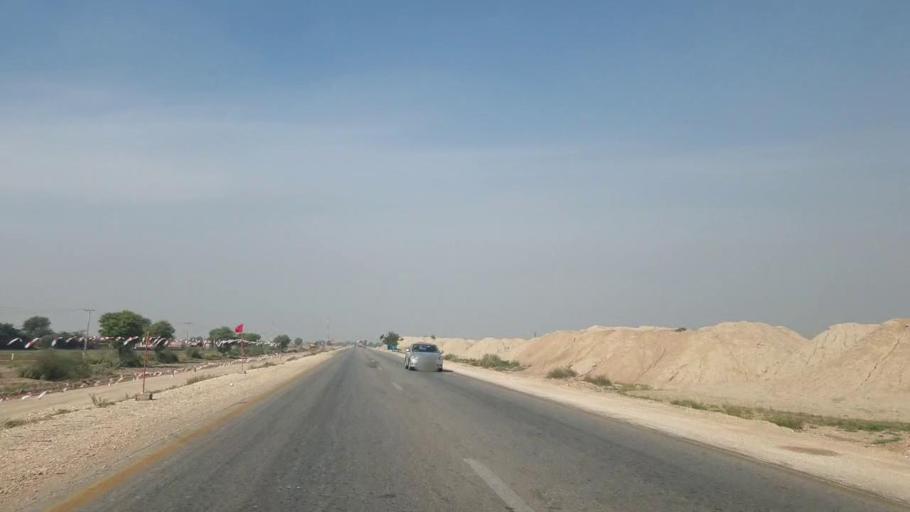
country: PK
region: Sindh
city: Sann
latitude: 25.9715
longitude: 68.1880
